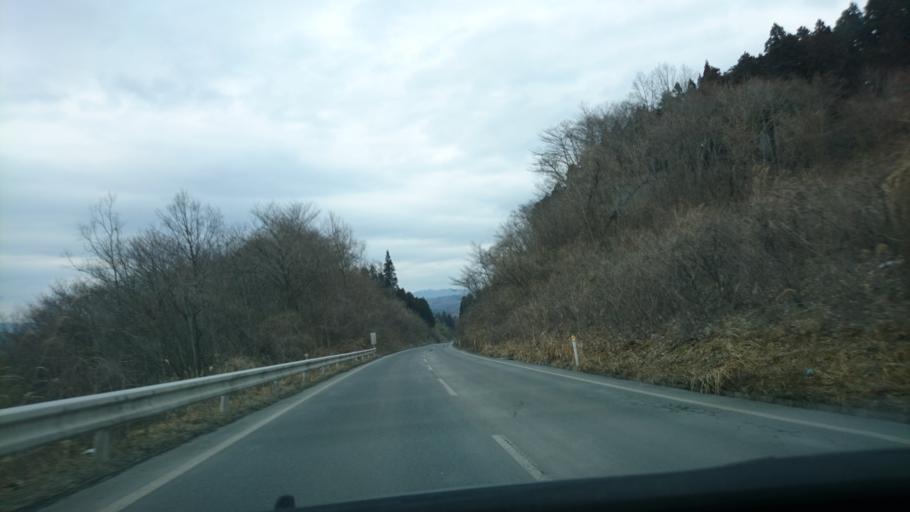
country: JP
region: Iwate
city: Ichinoseki
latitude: 38.9767
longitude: 141.3551
